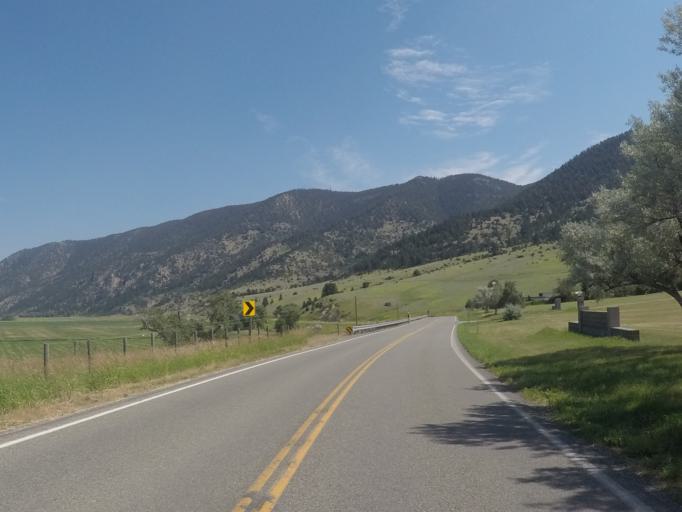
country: US
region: Montana
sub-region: Park County
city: Livingston
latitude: 45.5748
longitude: -110.5663
